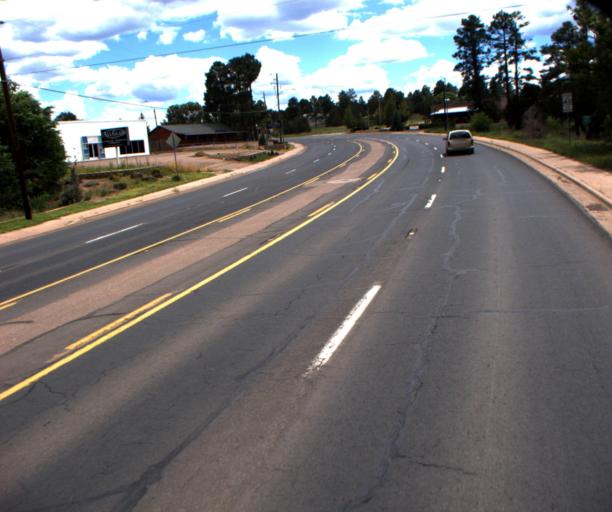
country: US
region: Arizona
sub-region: Navajo County
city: Show Low
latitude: 34.2484
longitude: -110.0285
